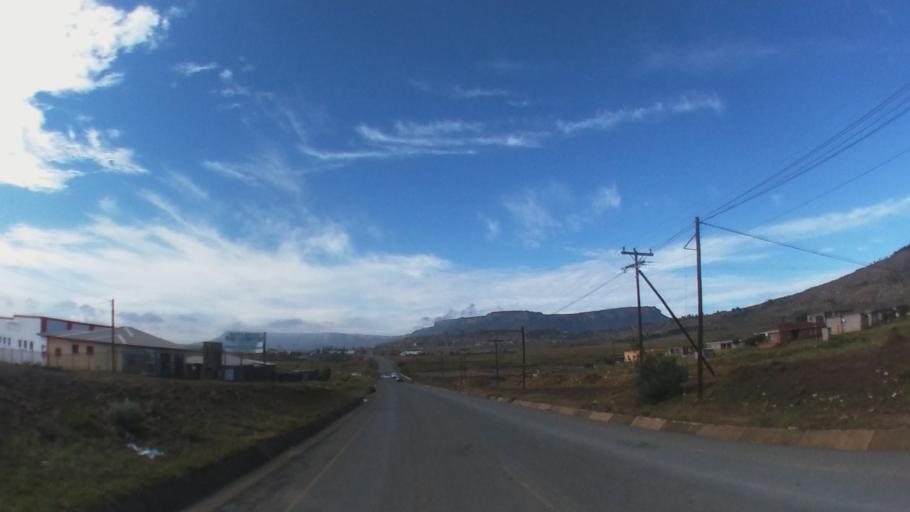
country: LS
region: Maseru
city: Maseru
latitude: -29.3751
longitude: 27.4706
